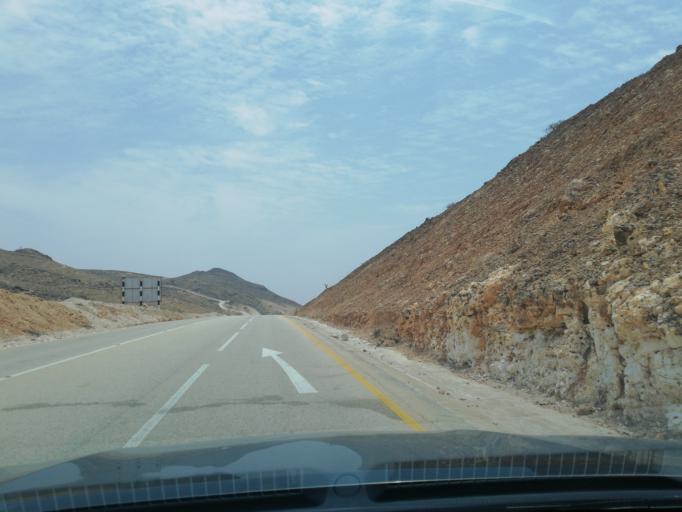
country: OM
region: Zufar
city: Salalah
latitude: 16.8759
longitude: 53.7307
